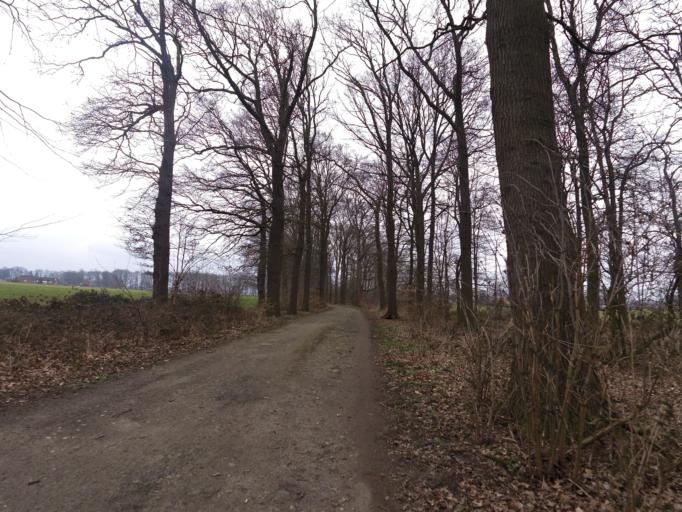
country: DE
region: North Rhine-Westphalia
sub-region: Regierungsbezirk Munster
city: Isselburg
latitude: 51.8621
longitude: 6.4289
